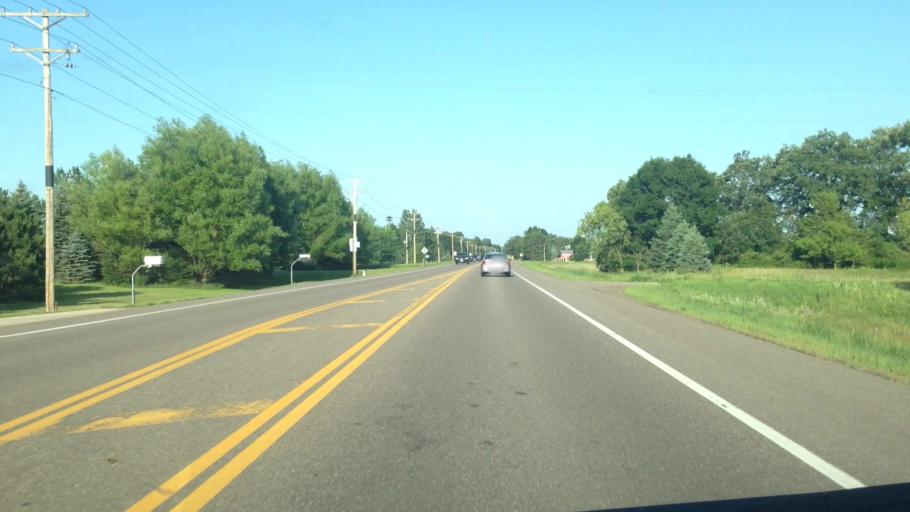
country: US
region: Minnesota
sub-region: Sherburne County
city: Zimmerman
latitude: 45.4436
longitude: -93.6127
